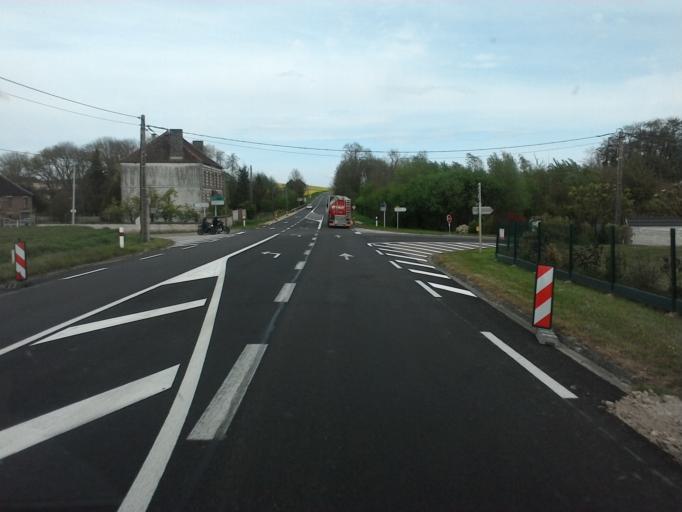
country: FR
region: Champagne-Ardenne
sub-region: Departement de l'Aube
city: Bouilly
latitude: 48.1261
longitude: 3.9636
